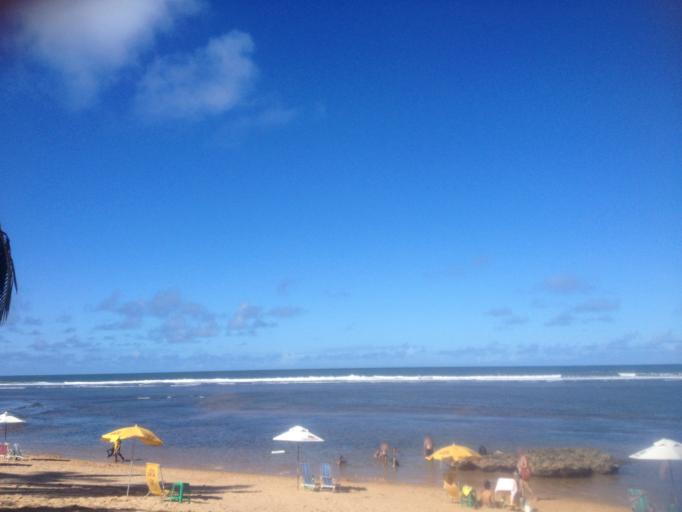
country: BR
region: Bahia
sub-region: Mata De Sao Joao
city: Mata de Sao Joao
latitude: -12.5742
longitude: -37.9998
